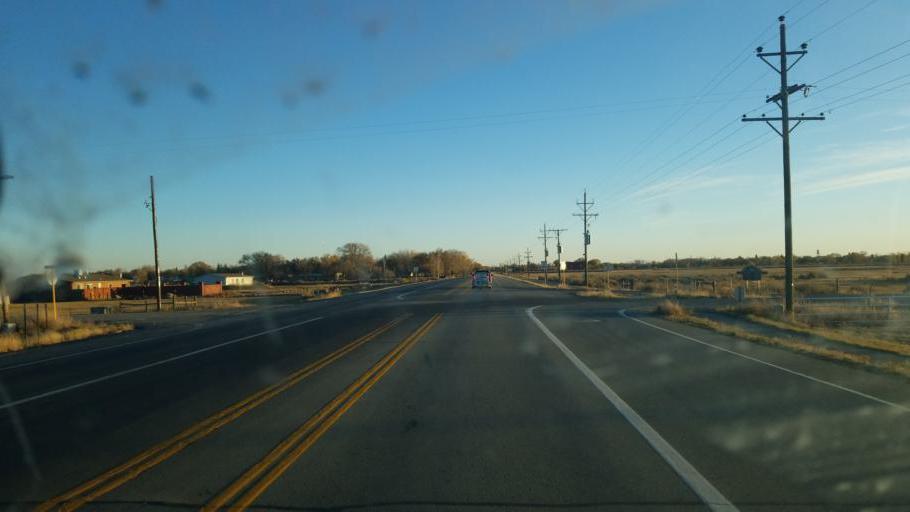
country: US
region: Colorado
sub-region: Alamosa County
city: Alamosa East
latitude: 37.4883
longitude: -105.8574
